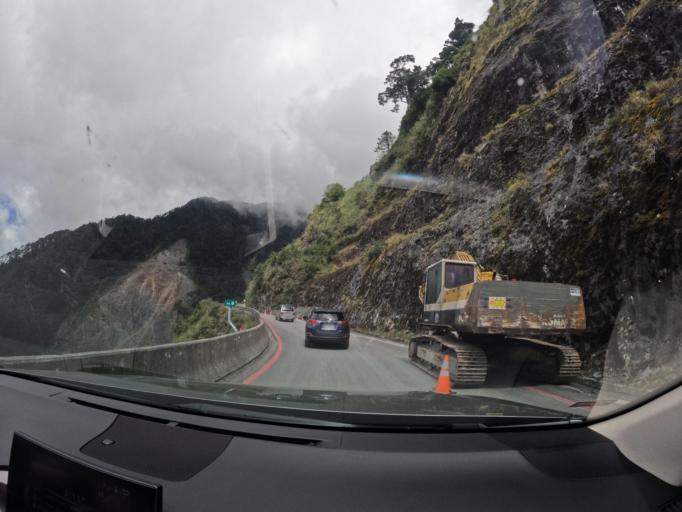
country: TW
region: Taiwan
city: Yujing
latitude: 23.2654
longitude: 120.9509
